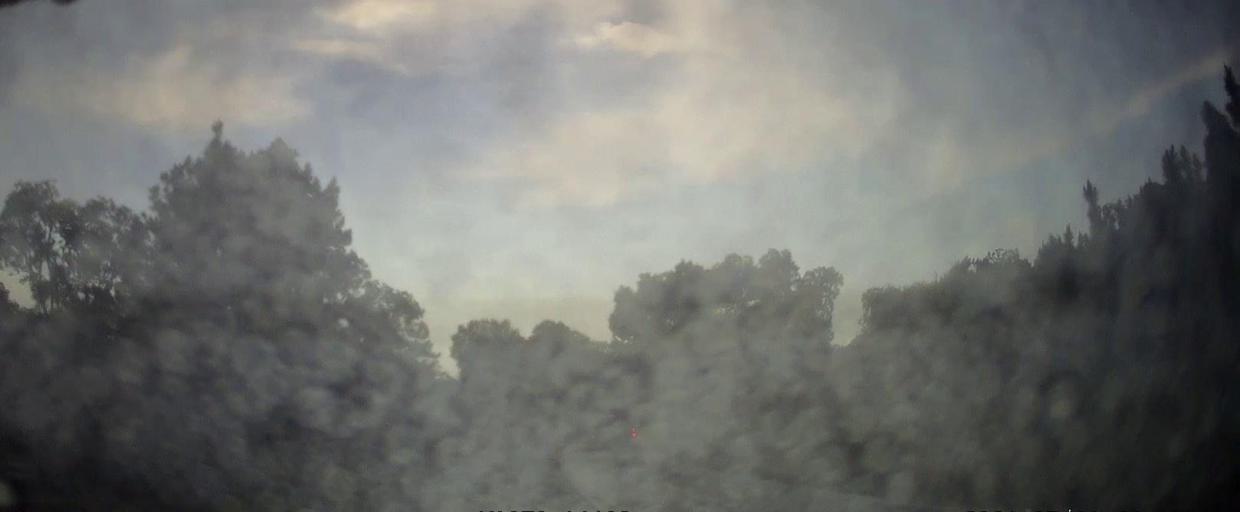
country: US
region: Georgia
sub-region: Dodge County
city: Chester
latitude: 32.5548
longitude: -83.1469
